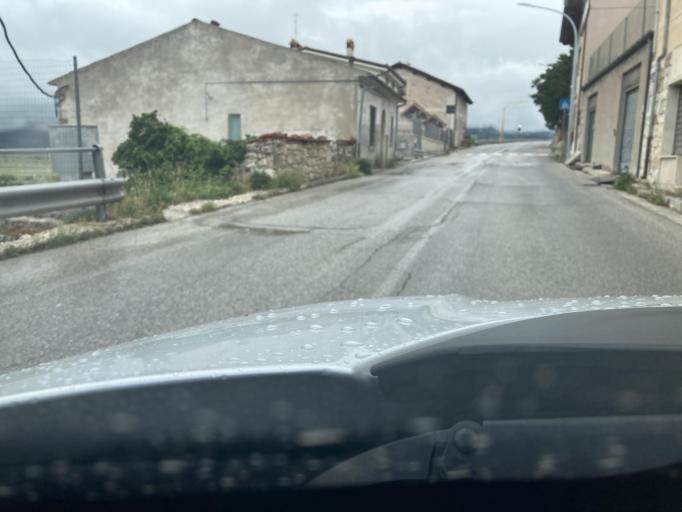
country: IT
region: Abruzzo
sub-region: Provincia dell' Aquila
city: Rocca di Mezzo
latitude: 42.2353
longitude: 13.5332
